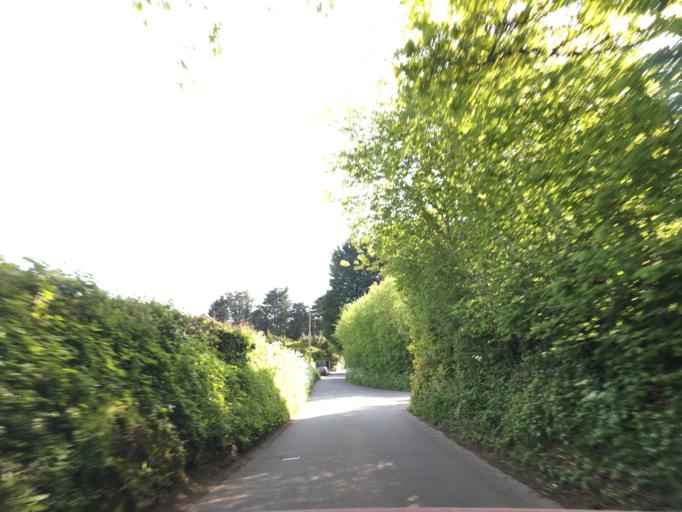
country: GB
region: Wales
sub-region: Newport
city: Marshfield
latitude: 51.5355
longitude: -3.1077
